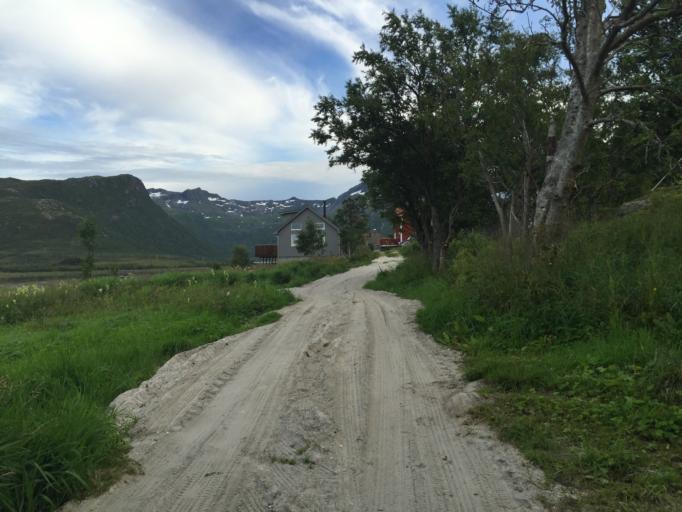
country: NO
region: Nordland
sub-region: Vagan
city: Kabelvag
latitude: 68.3278
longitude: 14.3967
